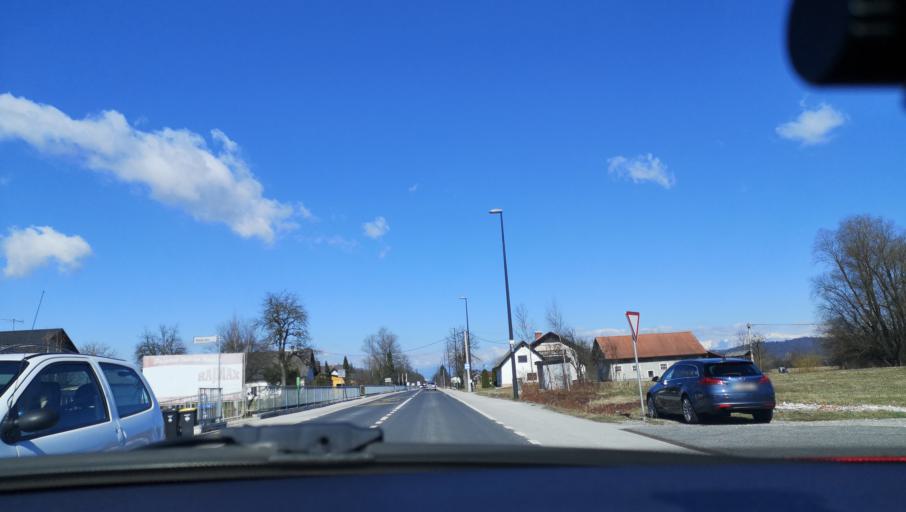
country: SI
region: Skofljica
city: Lavrica
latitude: 45.9995
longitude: 14.5169
